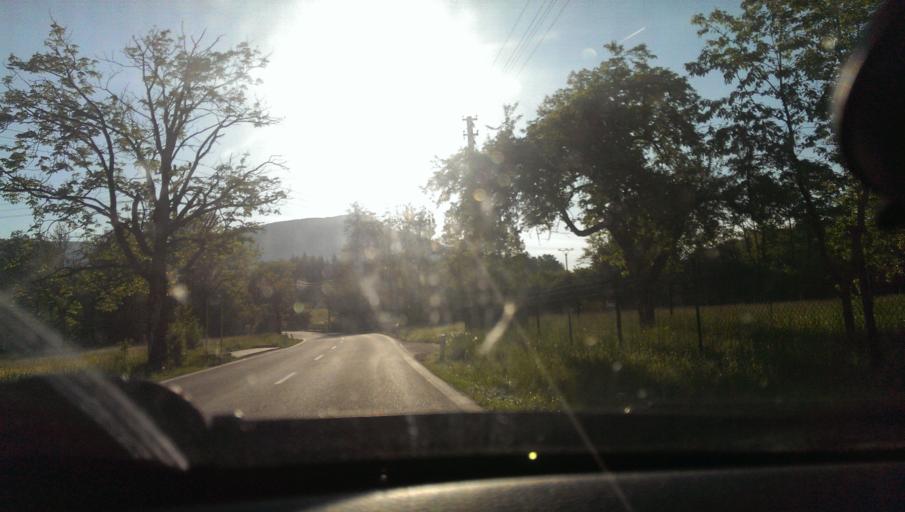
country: CZ
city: Kuncice pod Ondrejnikem
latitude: 49.5483
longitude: 18.2487
